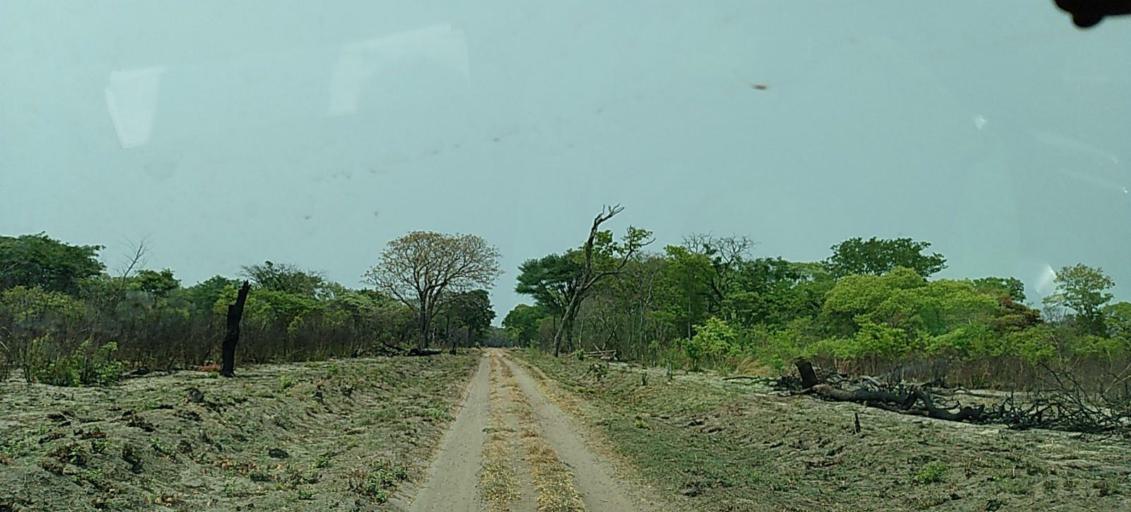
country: ZM
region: North-Western
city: Zambezi
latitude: -13.9474
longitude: 23.2236
